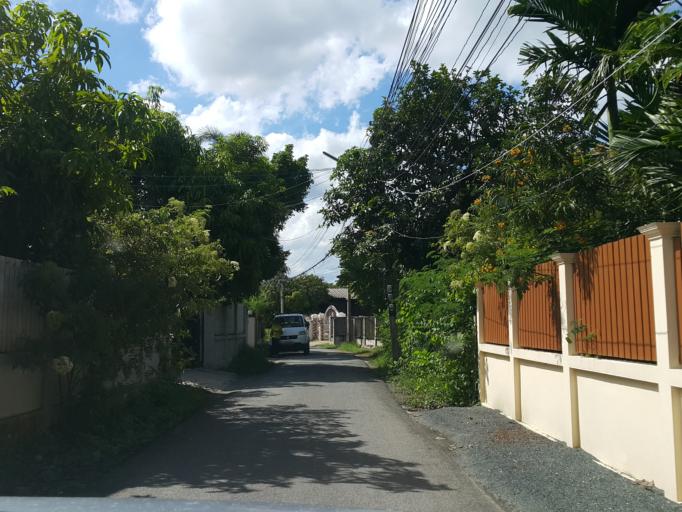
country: TH
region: Chiang Mai
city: San Kamphaeng
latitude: 18.7564
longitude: 99.1305
